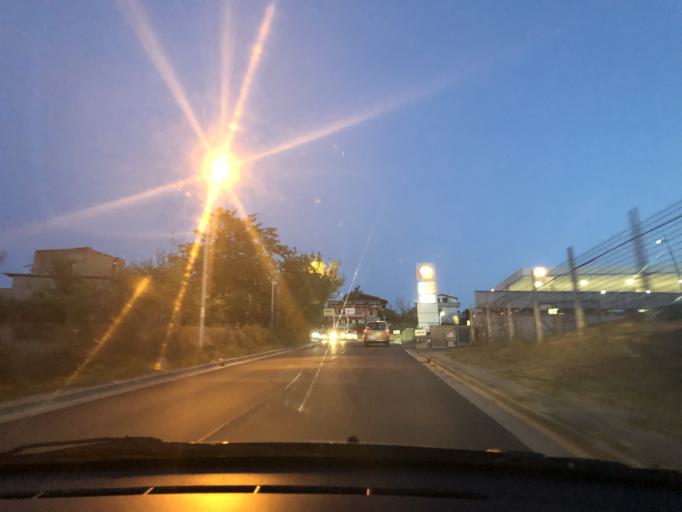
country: IT
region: Campania
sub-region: Provincia di Napoli
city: Marano di Napoli
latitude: 40.8896
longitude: 14.1792
